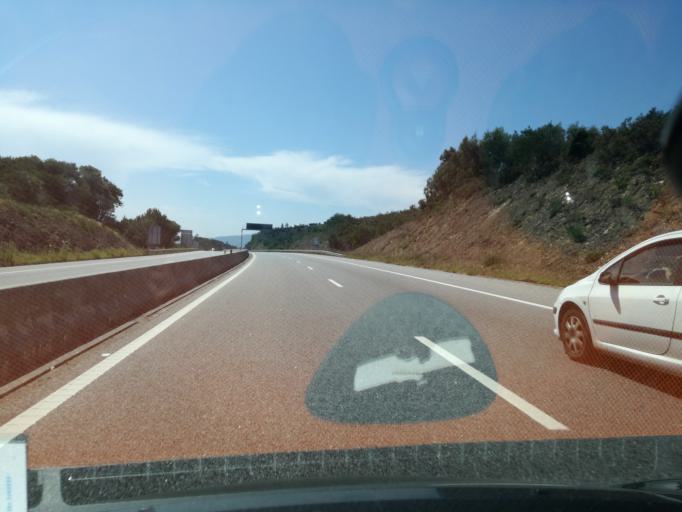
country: PT
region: Viana do Castelo
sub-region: Caminha
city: Vila Praia de Ancora
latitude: 41.8357
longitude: -8.7861
